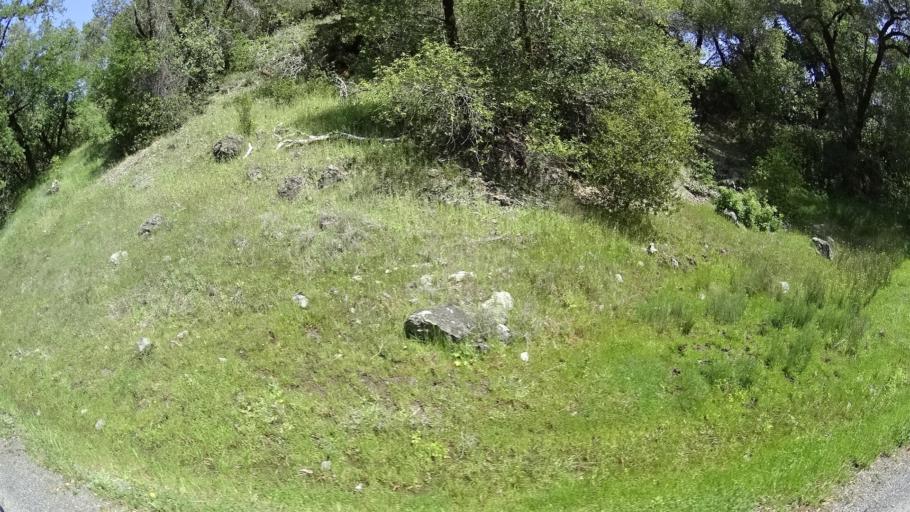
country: US
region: California
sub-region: Humboldt County
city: Redway
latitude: 40.2291
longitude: -123.6119
